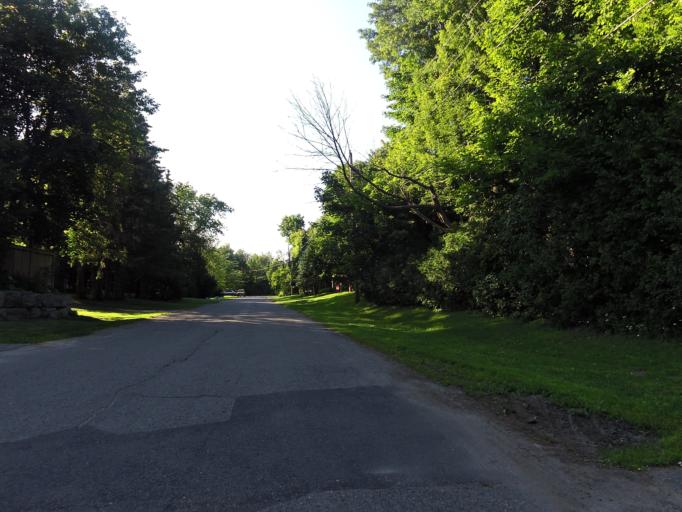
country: CA
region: Ontario
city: Ottawa
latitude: 45.3434
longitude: -75.6981
